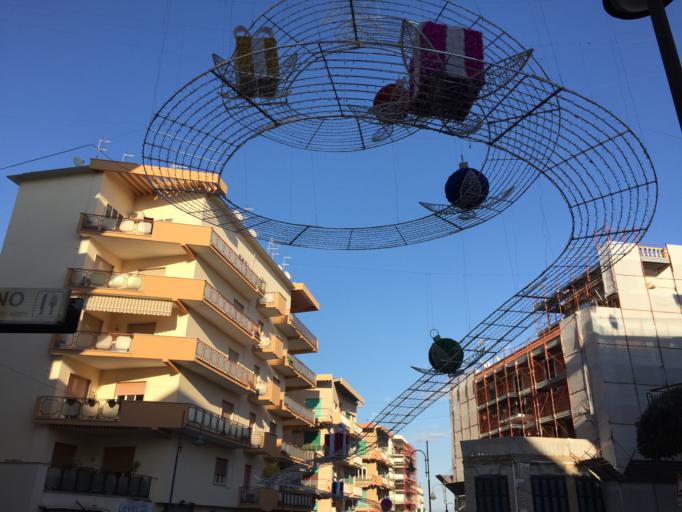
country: IT
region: Latium
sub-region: Provincia di Latina
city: Gaeta
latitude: 41.2142
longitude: 13.5683
